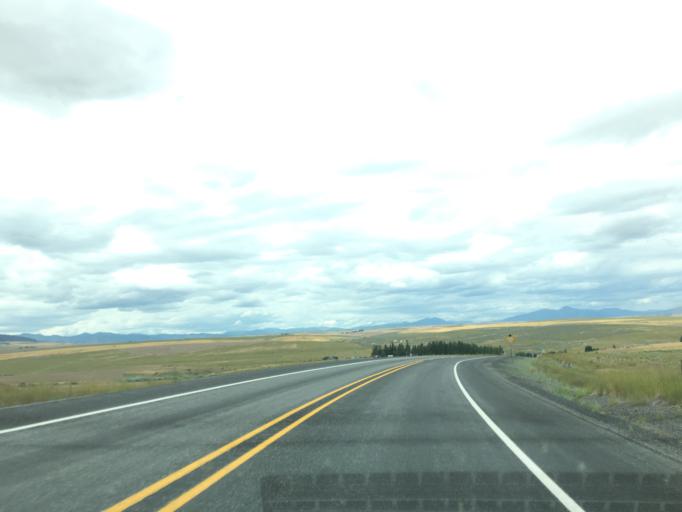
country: US
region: Washington
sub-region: Douglas County
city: Waterville
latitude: 47.6133
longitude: -119.9991
